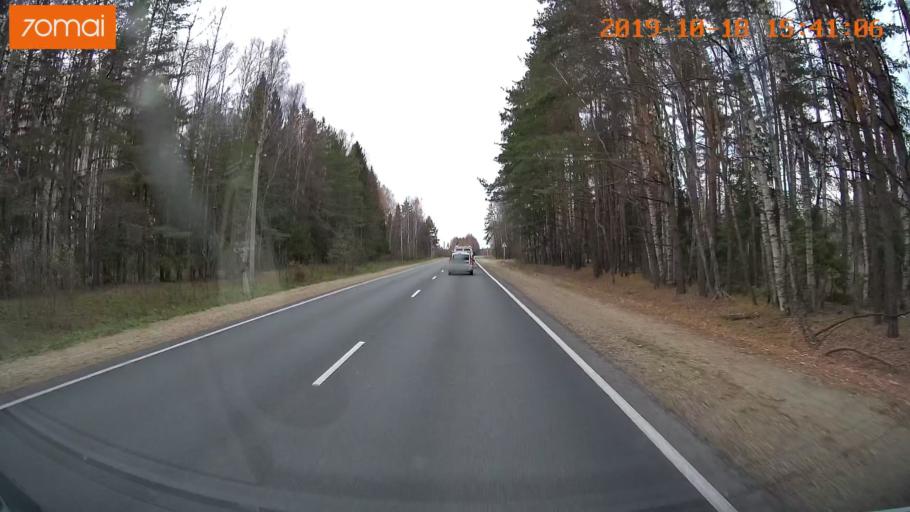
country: RU
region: Vladimir
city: Golovino
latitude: 55.9418
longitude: 40.5874
